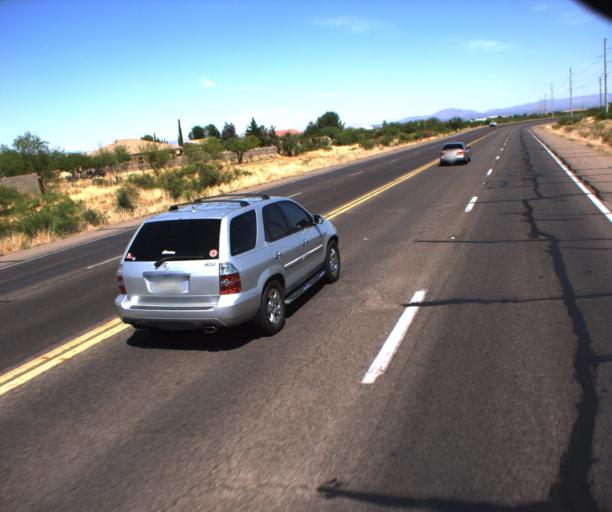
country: US
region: Arizona
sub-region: Cochise County
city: Sierra Vista
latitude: 31.5694
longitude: -110.2640
